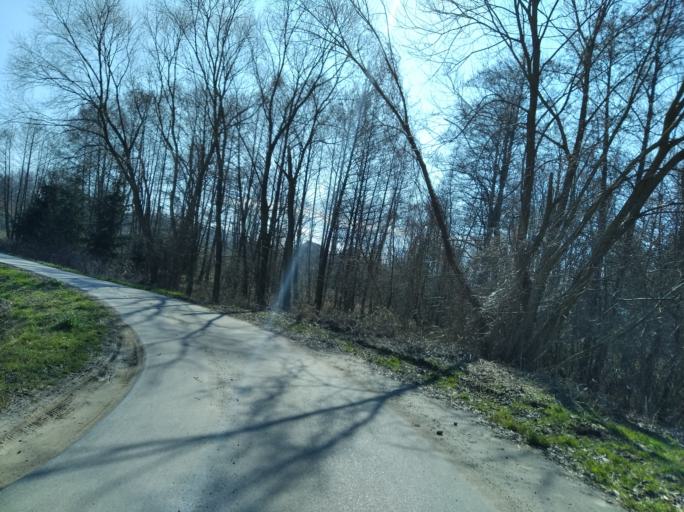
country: PL
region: Subcarpathian Voivodeship
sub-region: Powiat strzyzowski
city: Wysoka Strzyzowska
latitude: 49.8285
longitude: 21.7440
